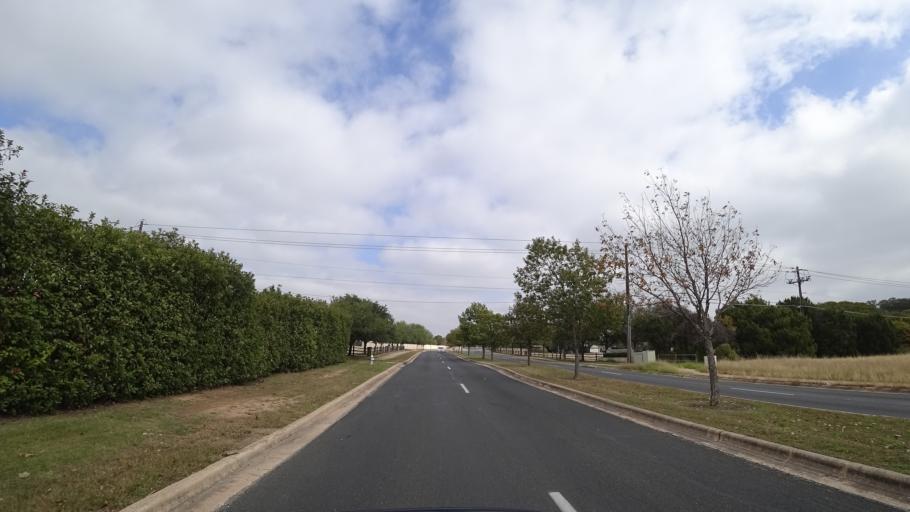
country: US
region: Texas
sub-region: Travis County
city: Shady Hollow
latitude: 30.1827
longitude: -97.8394
